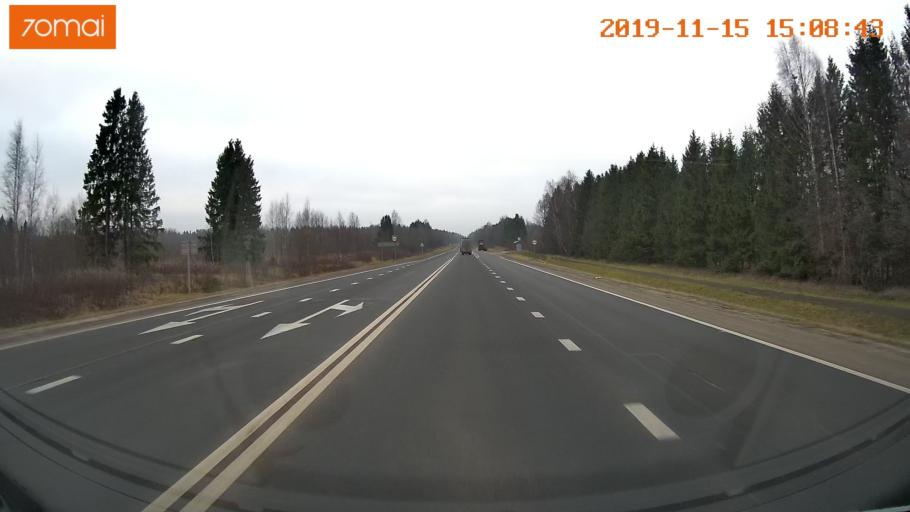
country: RU
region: Jaroslavl
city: Prechistoye
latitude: 58.3669
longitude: 40.2730
